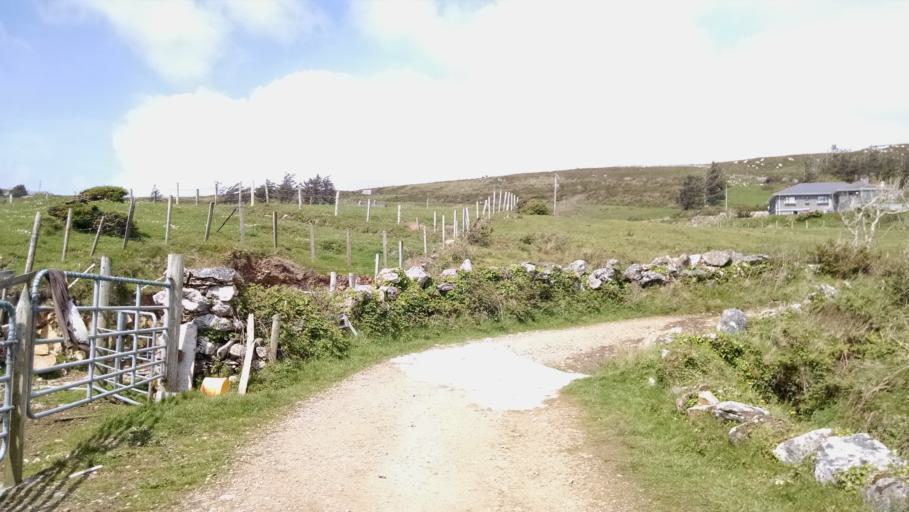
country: IE
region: Connaught
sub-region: County Galway
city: Clifden
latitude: 53.4919
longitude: -10.0536
